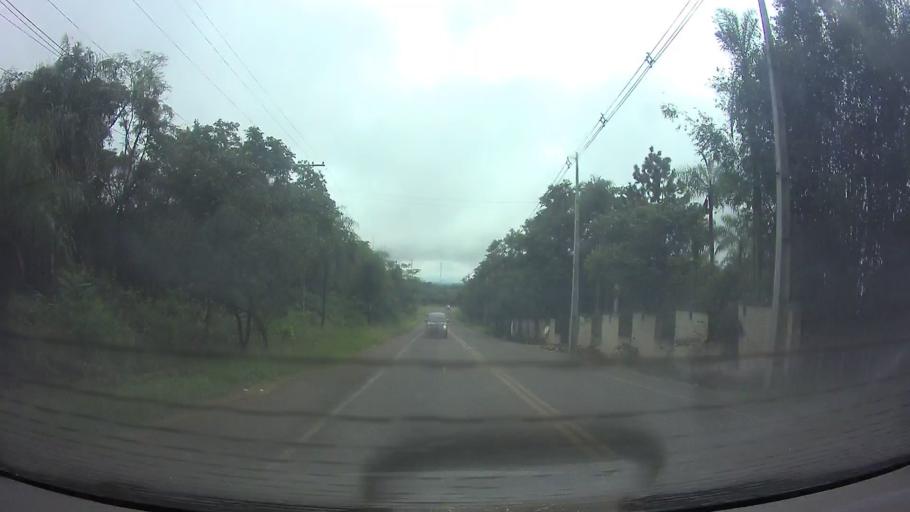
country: PY
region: Cordillera
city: Altos
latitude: -25.2843
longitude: -57.2622
